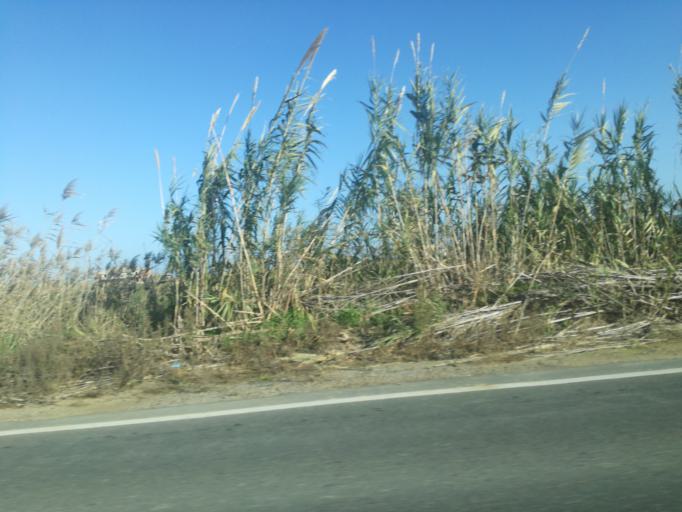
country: IT
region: Sicily
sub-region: Provincia di Caltanissetta
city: Gela
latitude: 37.0538
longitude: 14.3043
